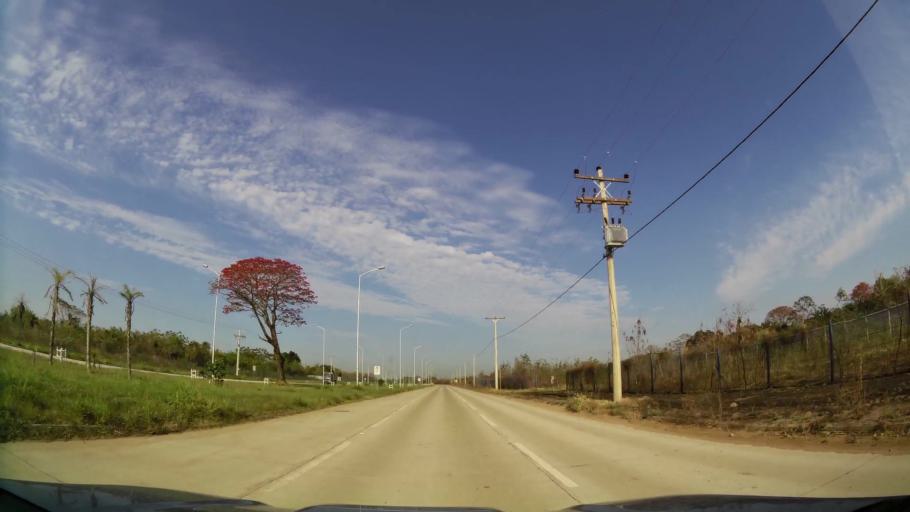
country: BO
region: Santa Cruz
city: Santa Cruz de la Sierra
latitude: -17.6929
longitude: -63.1182
